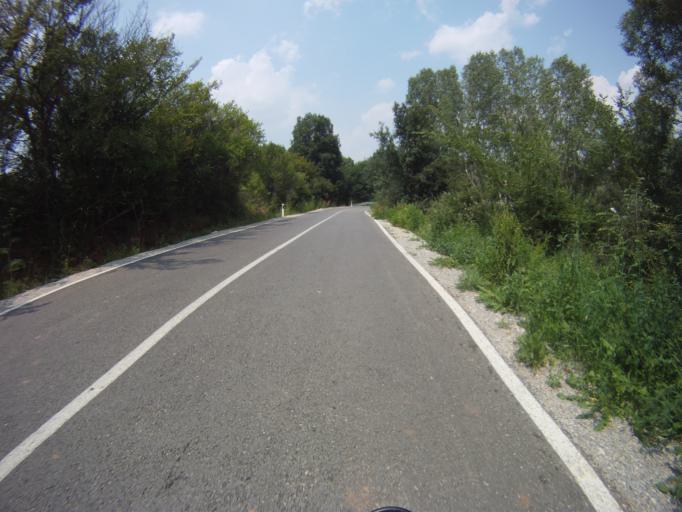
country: RS
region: Central Serbia
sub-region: Nisavski Okrug
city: Gadzin Han
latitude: 43.2076
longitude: 22.0134
